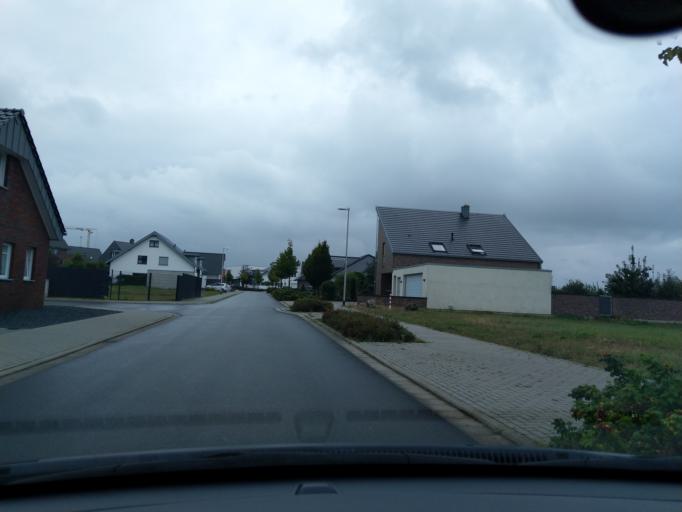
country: DE
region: North Rhine-Westphalia
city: Erkelenz
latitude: 51.0604
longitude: 6.3339
